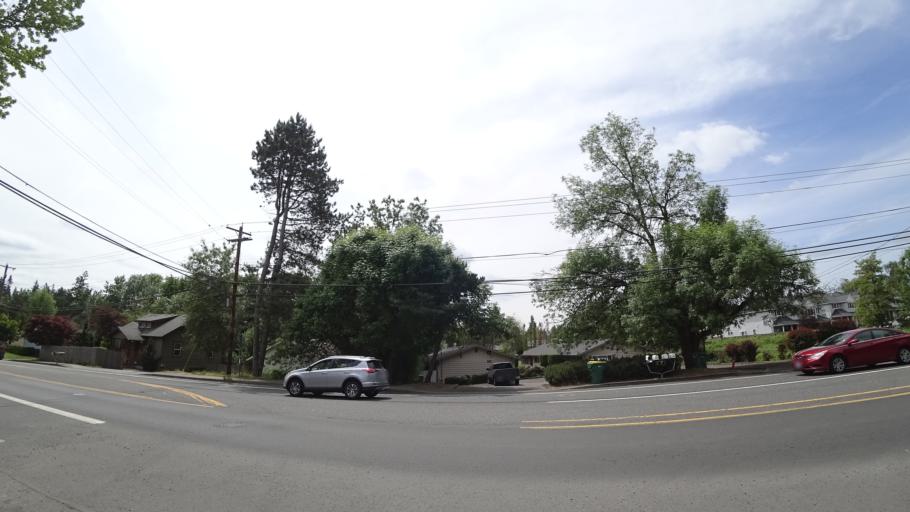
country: US
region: Oregon
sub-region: Washington County
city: Metzger
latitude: 45.4513
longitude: -122.7678
